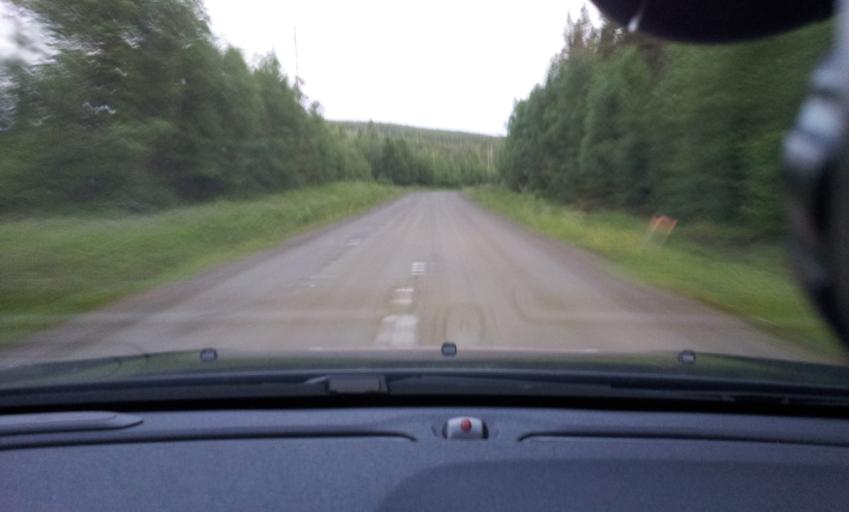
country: SE
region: Jaemtland
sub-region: Ragunda Kommun
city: Hammarstrand
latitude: 62.8742
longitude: 16.0579
